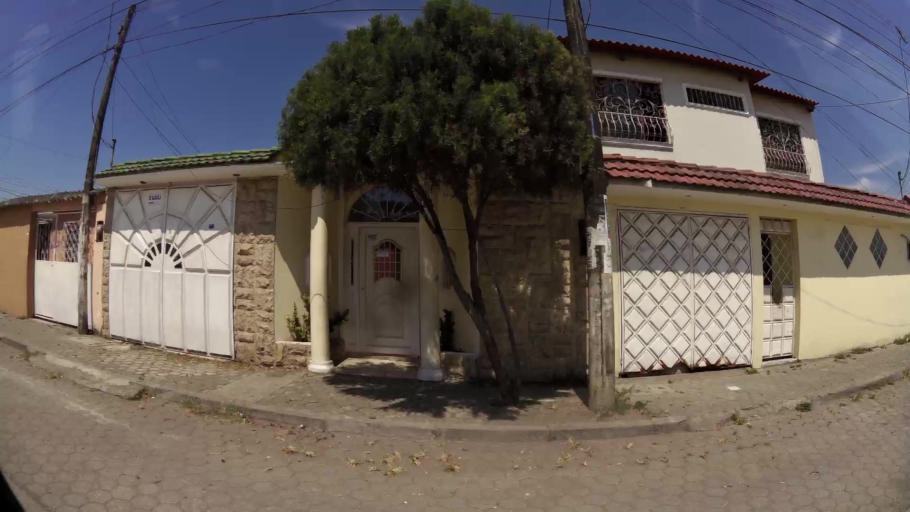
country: EC
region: Guayas
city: Eloy Alfaro
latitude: -2.1085
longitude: -79.9043
